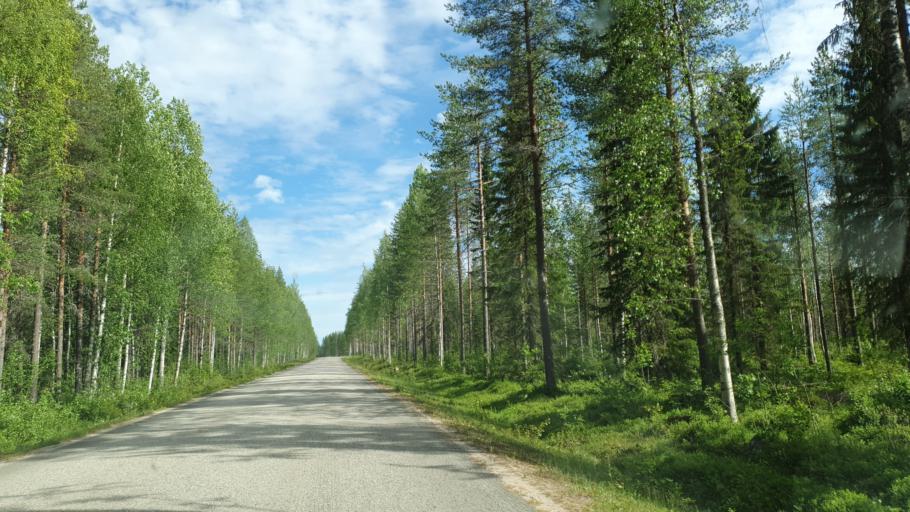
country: FI
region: Kainuu
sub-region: Kehys-Kainuu
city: Kuhmo
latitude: 64.5181
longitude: 29.3857
